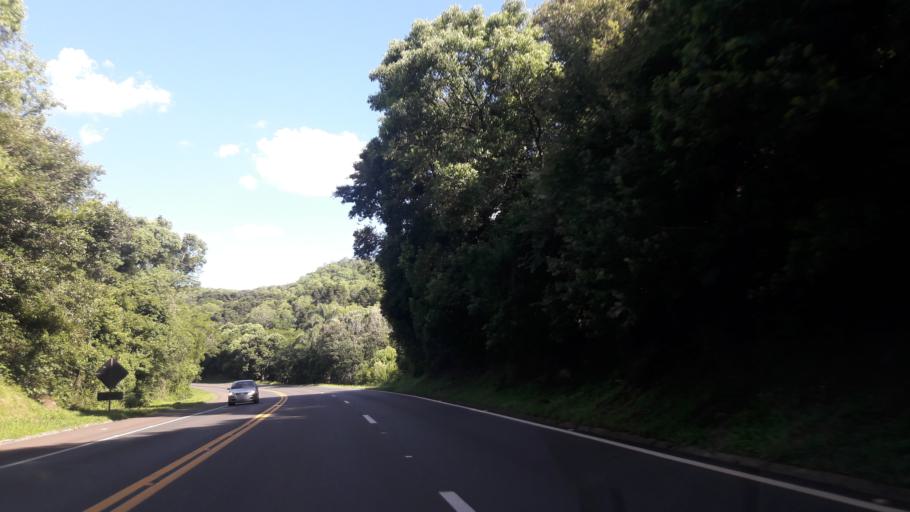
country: BR
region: Parana
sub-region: Laranjeiras Do Sul
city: Laranjeiras do Sul
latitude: -25.4181
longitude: -52.0565
